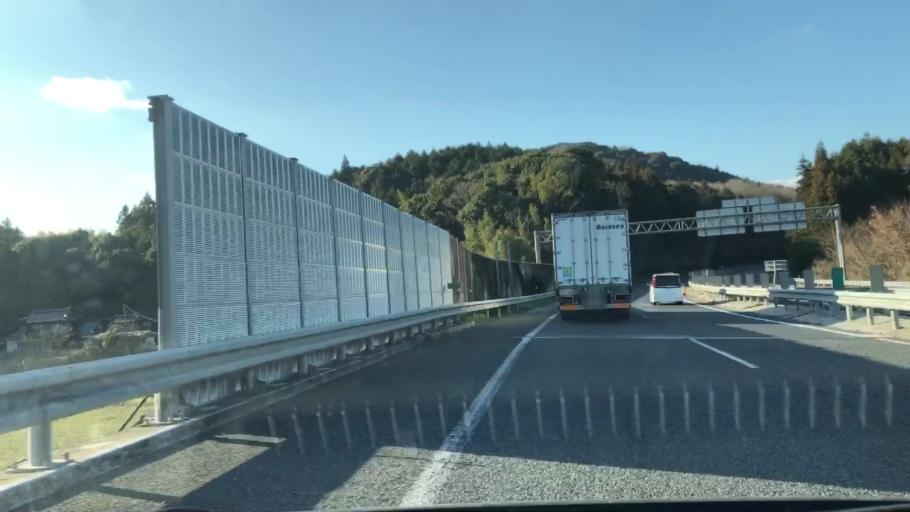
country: JP
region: Yamaguchi
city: Ogori-shimogo
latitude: 34.1729
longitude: 131.3130
